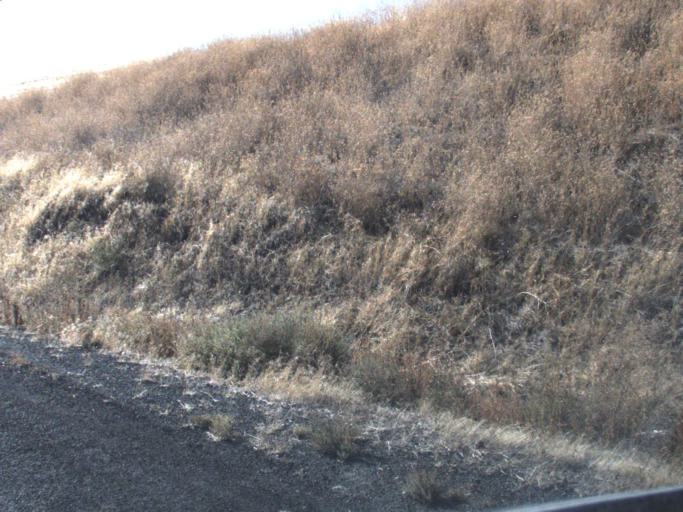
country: US
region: Washington
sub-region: Walla Walla County
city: Waitsburg
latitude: 46.2834
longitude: -118.3421
